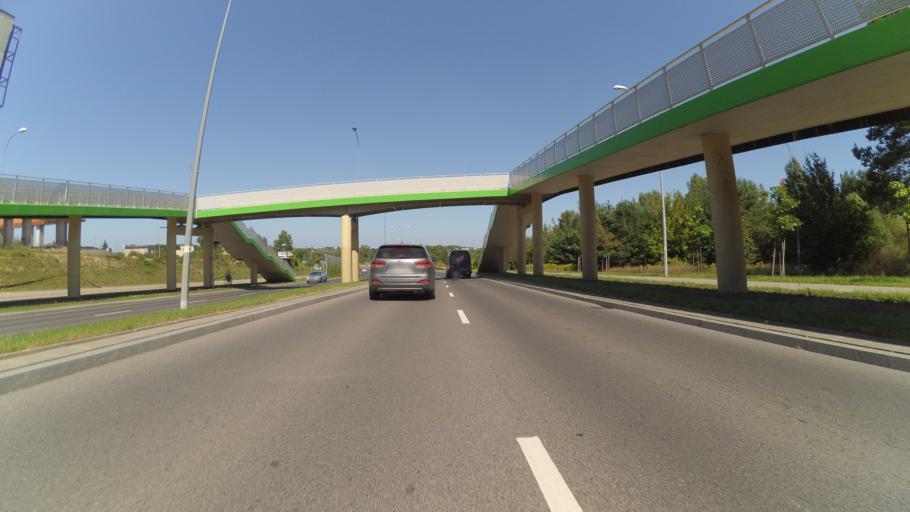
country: PL
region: Podlasie
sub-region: Bialystok
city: Bialystok
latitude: 53.1334
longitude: 23.2218
